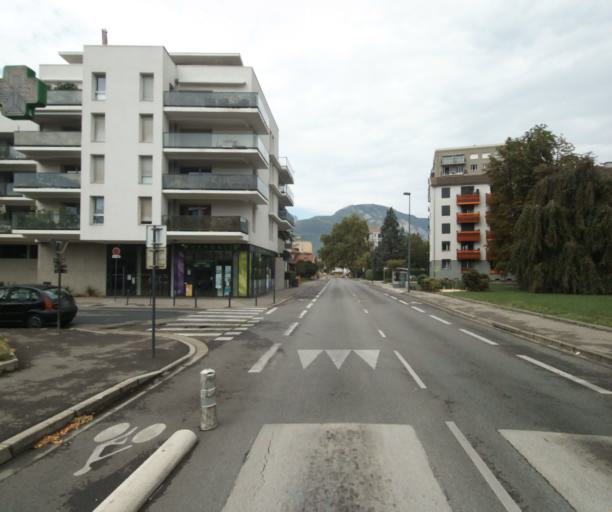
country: FR
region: Rhone-Alpes
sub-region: Departement de l'Isere
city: Saint-Martin-d'Heres
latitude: 45.1785
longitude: 5.7426
